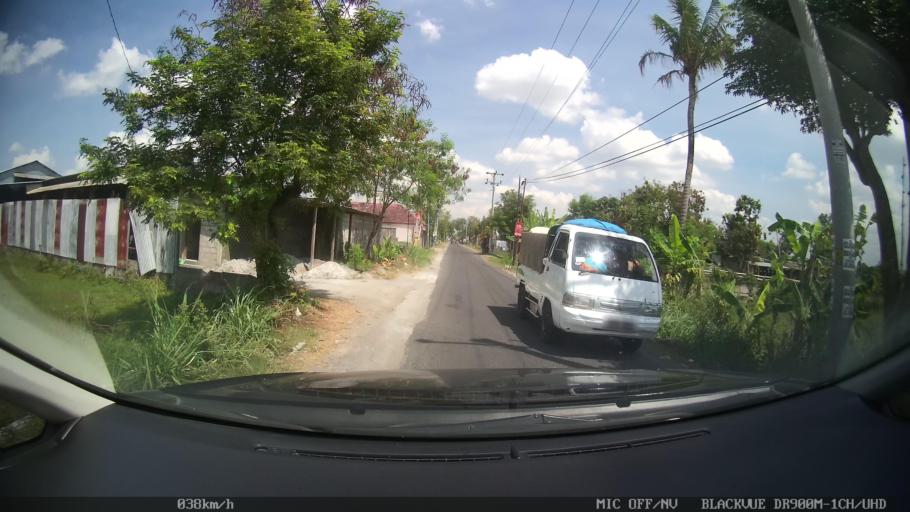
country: ID
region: Daerah Istimewa Yogyakarta
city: Sewon
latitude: -7.8433
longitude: 110.3869
